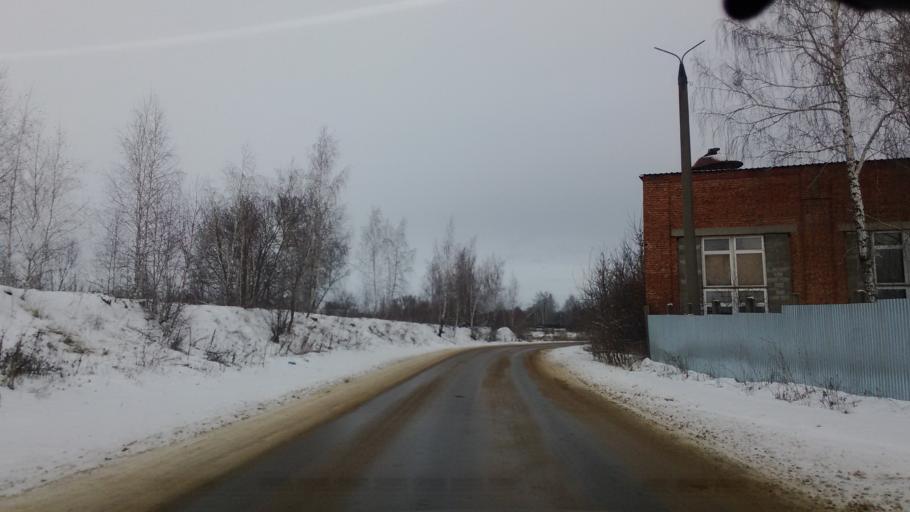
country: RU
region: Tula
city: Bogoroditsk
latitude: 53.7610
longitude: 38.1056
